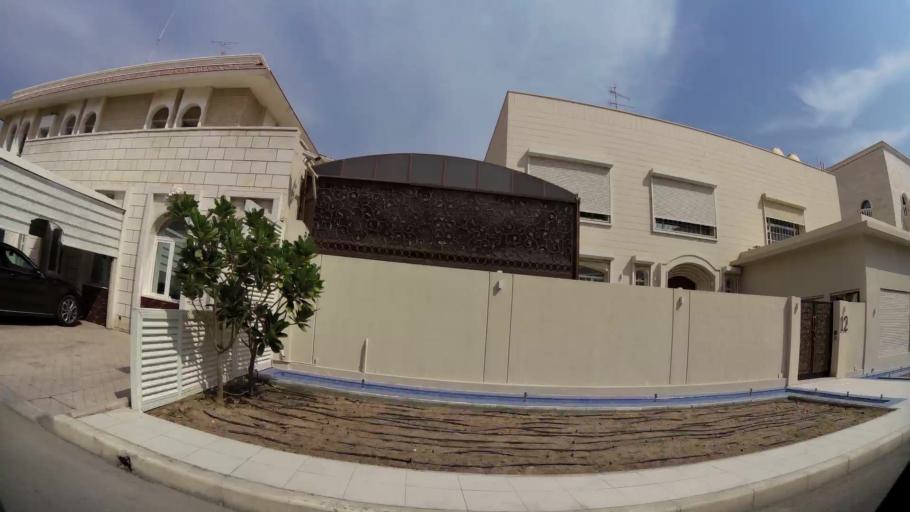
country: KW
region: Al Asimah
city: Ad Dasmah
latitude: 29.3532
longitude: 47.9897
